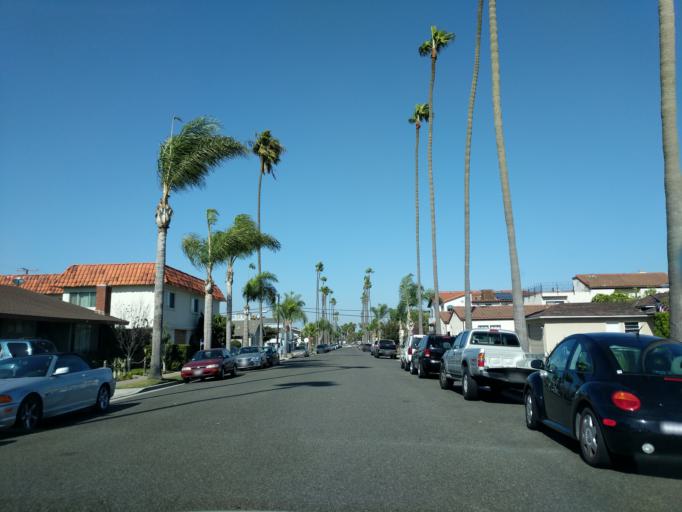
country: US
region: California
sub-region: Orange County
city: Seal Beach
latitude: 33.7421
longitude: -118.1079
